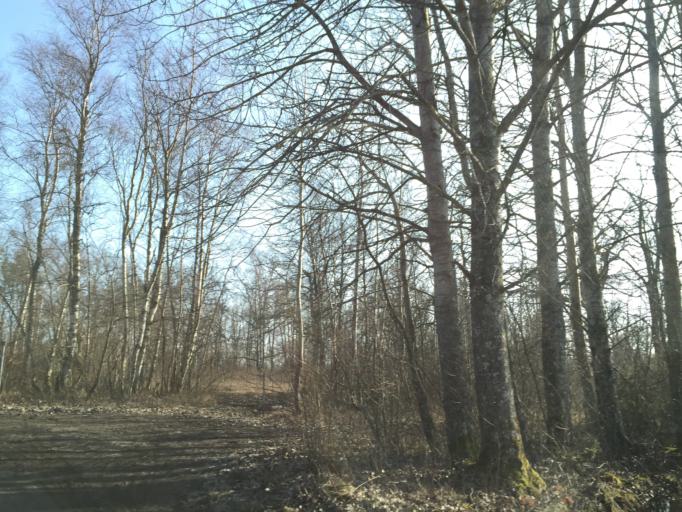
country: EE
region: Saare
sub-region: Kuressaare linn
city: Kuressaare
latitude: 58.2352
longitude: 22.4458
